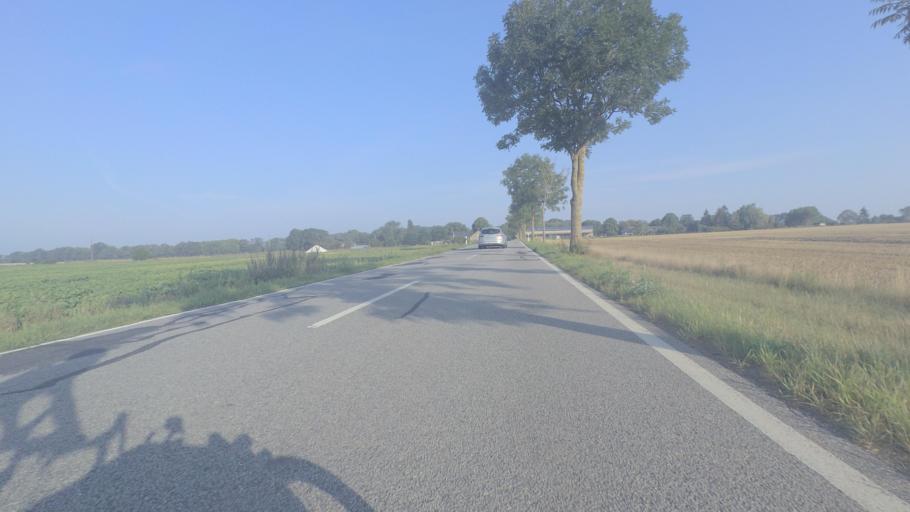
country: DE
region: Mecklenburg-Vorpommern
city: Demmin
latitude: 53.9511
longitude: 13.1151
